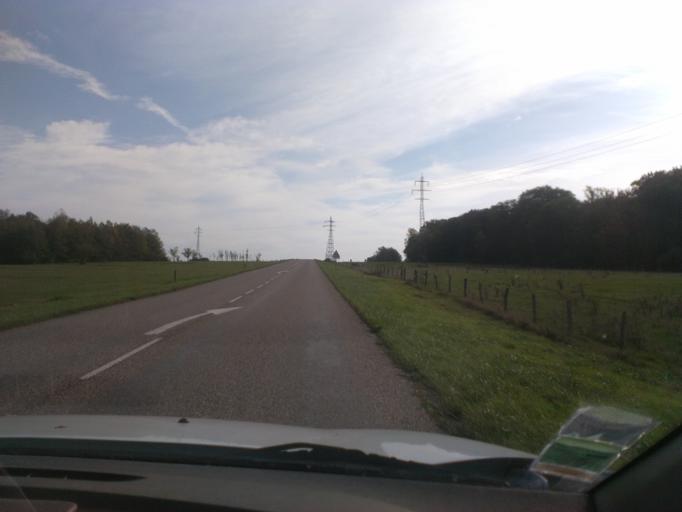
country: FR
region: Lorraine
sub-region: Departement des Vosges
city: Chatel-sur-Moselle
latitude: 48.3439
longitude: 6.4472
